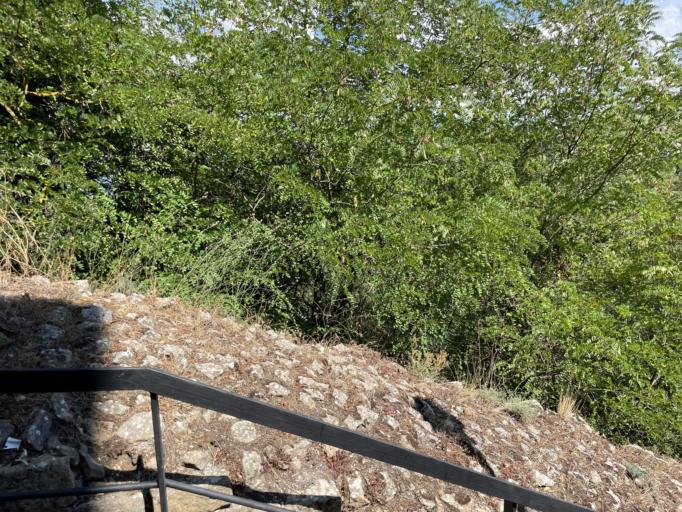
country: IT
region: Tuscany
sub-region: Province of Pisa
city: Volterra
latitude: 43.4032
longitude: 10.8628
